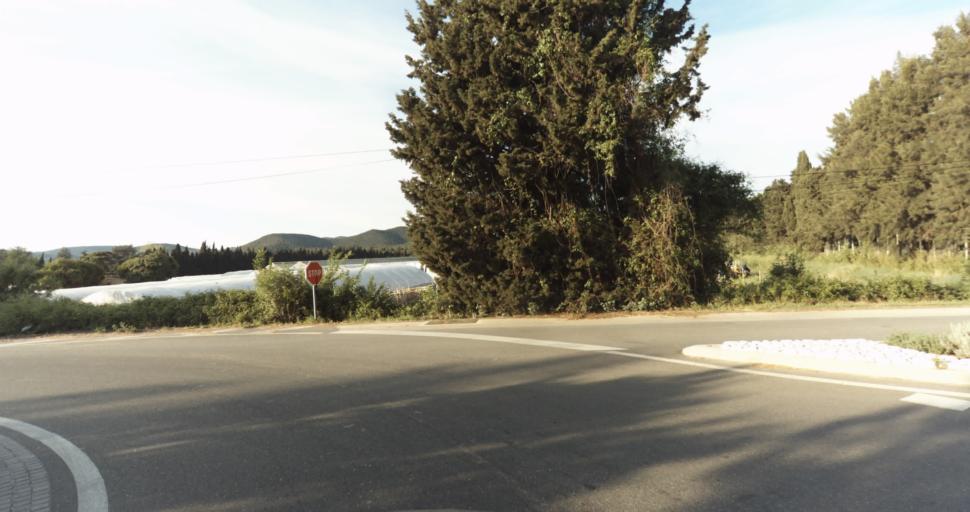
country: FR
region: Provence-Alpes-Cote d'Azur
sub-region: Departement du Var
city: Hyeres
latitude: 43.1308
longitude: 6.1666
